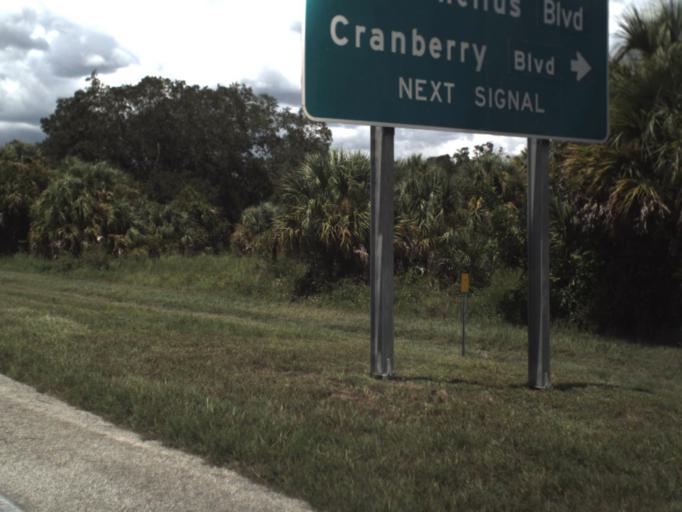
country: US
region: Florida
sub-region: Sarasota County
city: North Port
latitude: 27.0312
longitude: -82.2024
